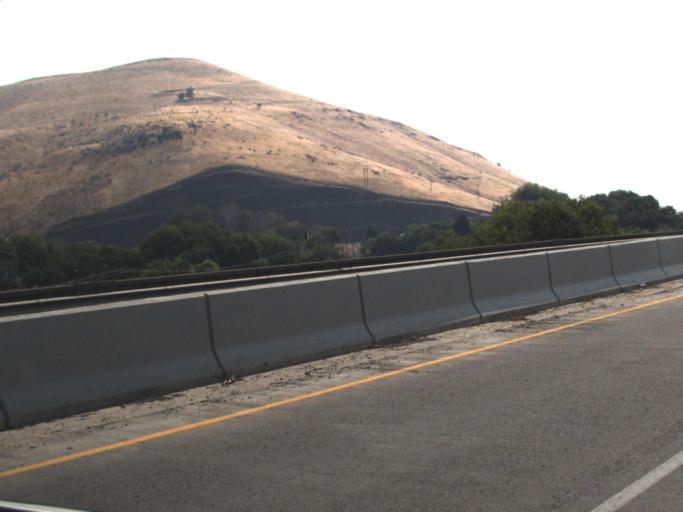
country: US
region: Washington
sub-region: Yakima County
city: Selah
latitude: 46.6394
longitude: -120.5291
